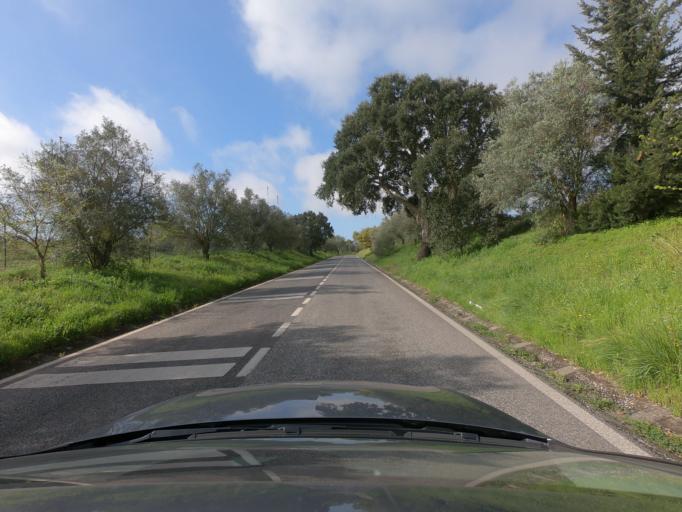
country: PT
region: Lisbon
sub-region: Oeiras
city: Quejas
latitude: 38.7266
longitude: -9.2704
